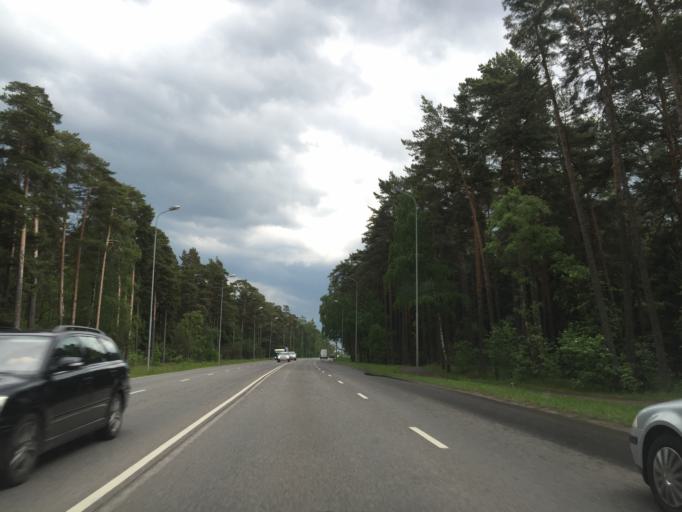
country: LT
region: Klaipedos apskritis
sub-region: Klaipeda
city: Klaipeda
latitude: 55.7331
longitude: 21.1137
